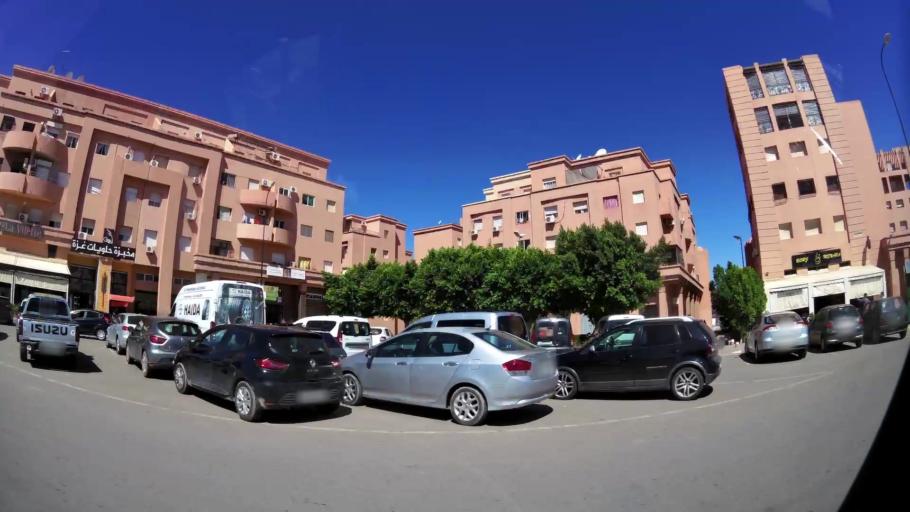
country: MA
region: Marrakech-Tensift-Al Haouz
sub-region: Marrakech
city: Marrakesh
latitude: 31.5801
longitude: -8.0539
